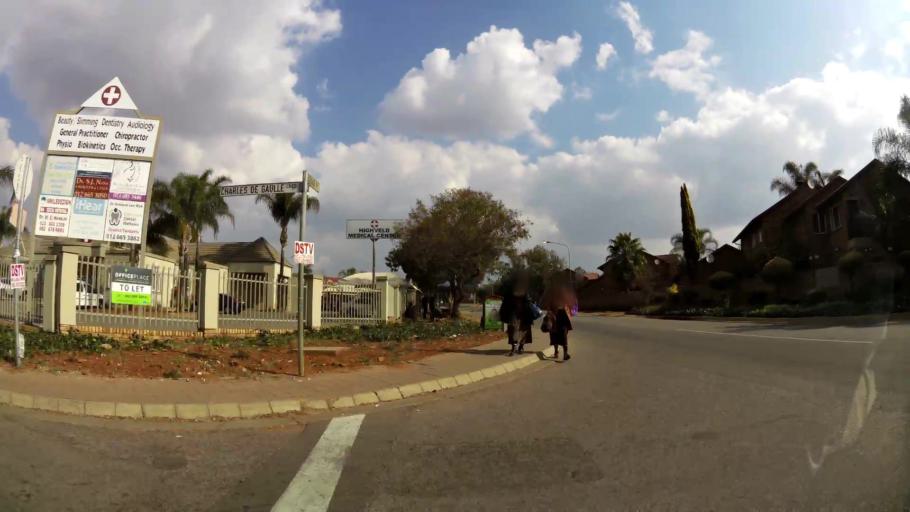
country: ZA
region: Gauteng
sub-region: City of Tshwane Metropolitan Municipality
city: Centurion
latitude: -25.8768
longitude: 28.1977
